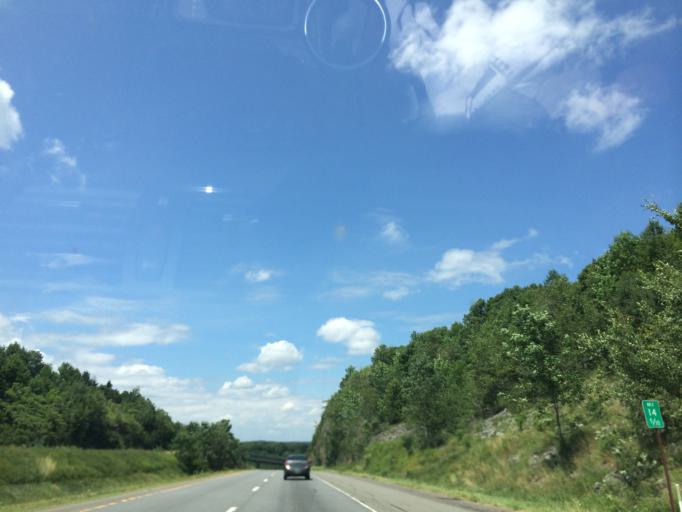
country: US
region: Pennsylvania
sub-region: Lackawanna County
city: Mount Cobb
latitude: 41.3557
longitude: -75.4153
